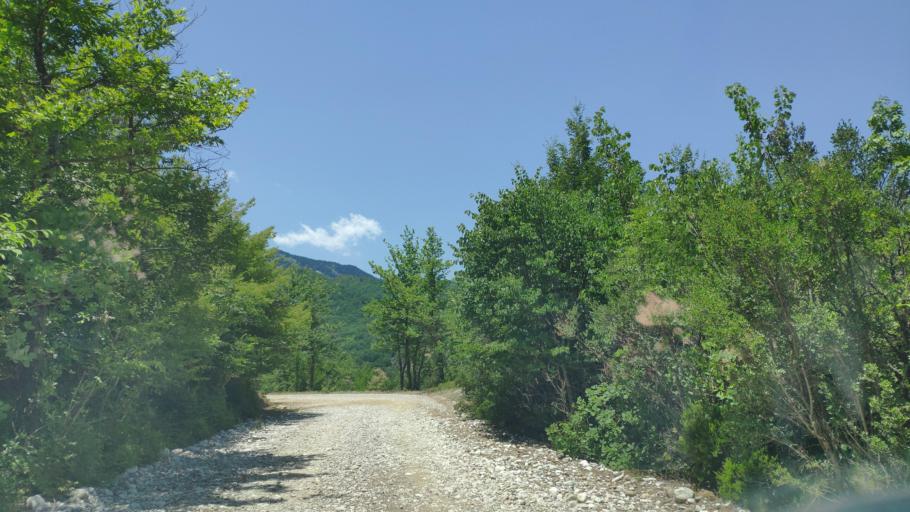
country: GR
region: Epirus
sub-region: Nomos Artas
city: Ano Kalentini
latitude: 39.1789
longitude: 21.3639
